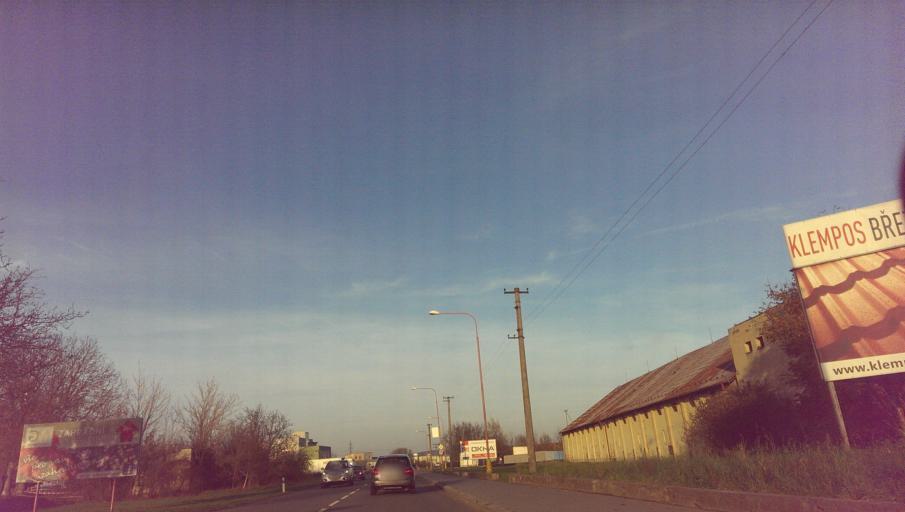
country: CZ
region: Zlin
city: Knezpole
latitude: 49.0878
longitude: 17.4973
